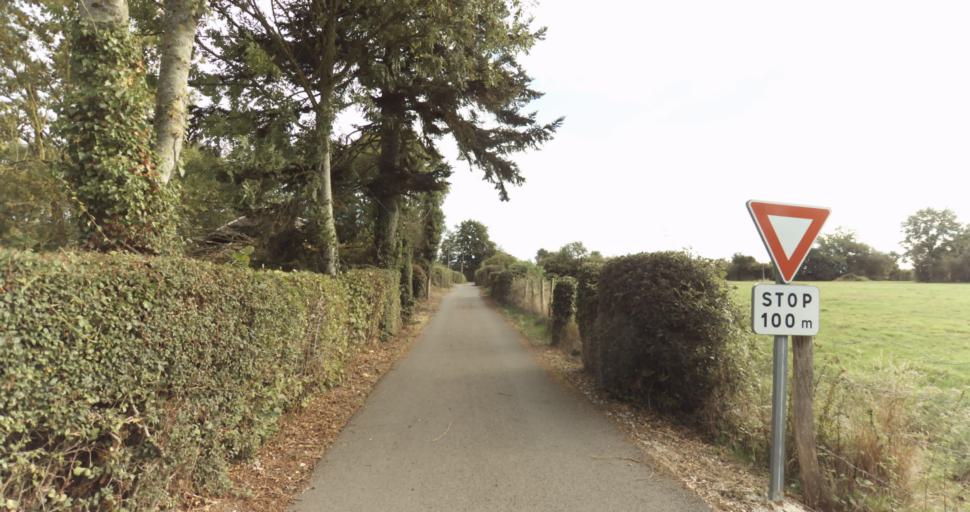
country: FR
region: Lower Normandy
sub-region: Departement de l'Orne
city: Gace
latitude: 48.8105
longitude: 0.2412
